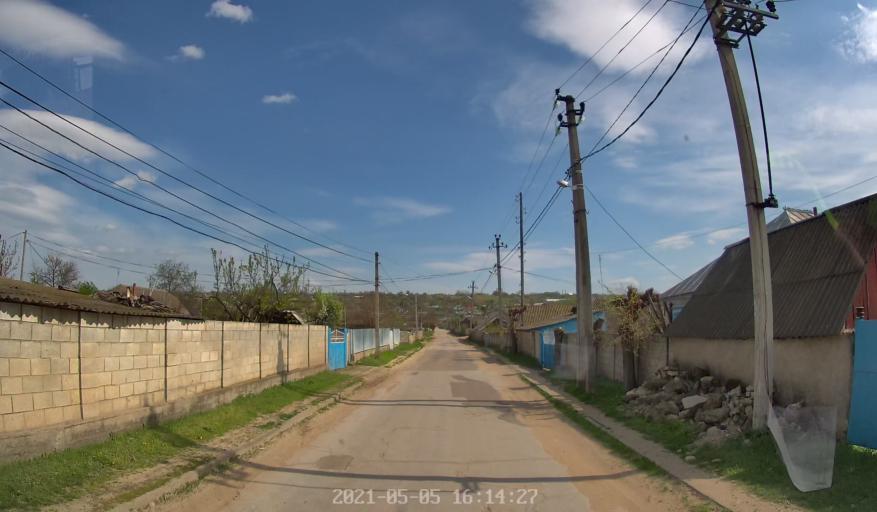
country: MD
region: Criuleni
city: Criuleni
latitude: 47.1374
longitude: 29.2006
